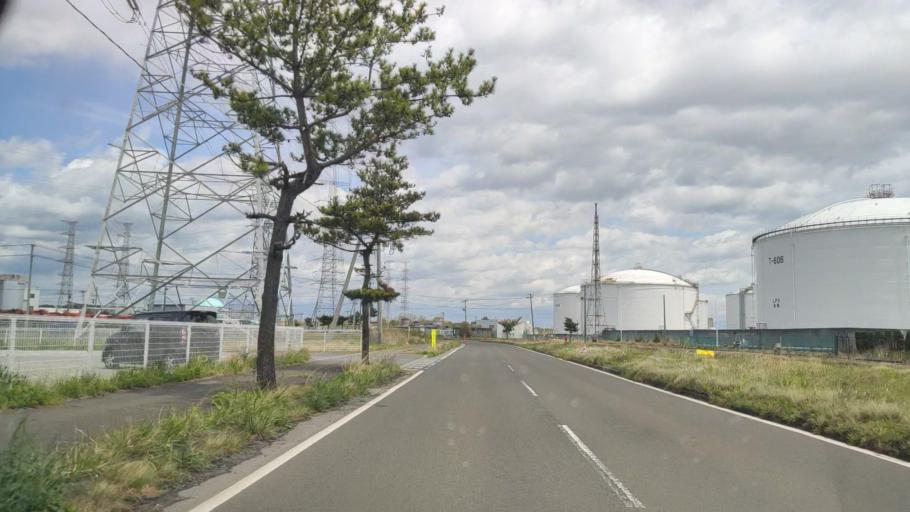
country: JP
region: Miyagi
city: Shiogama
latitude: 38.2812
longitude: 141.0233
